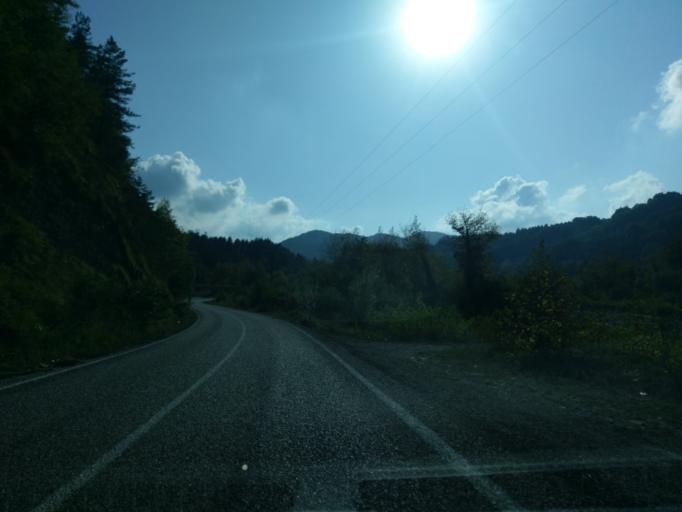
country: TR
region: Sinop
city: Yenikonak
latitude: 41.8794
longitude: 34.5563
